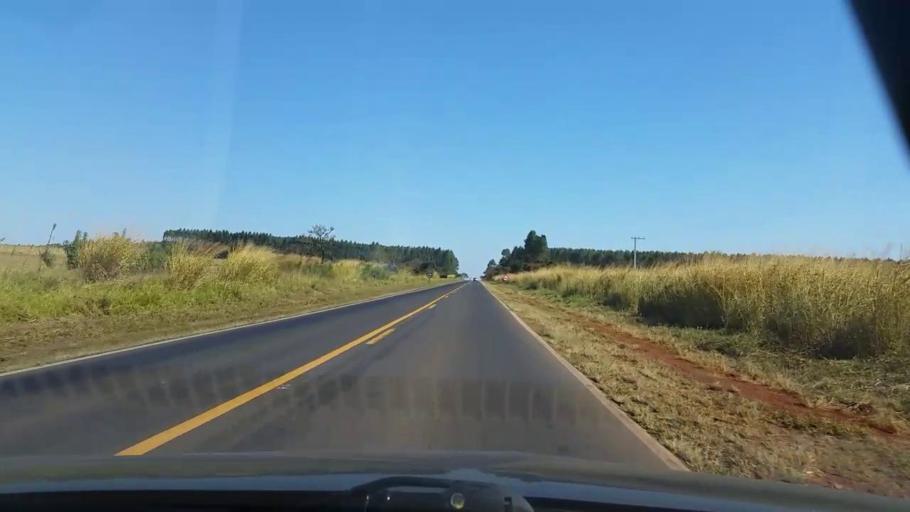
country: BR
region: Sao Paulo
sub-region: Avare
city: Avare
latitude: -22.9173
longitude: -48.7803
